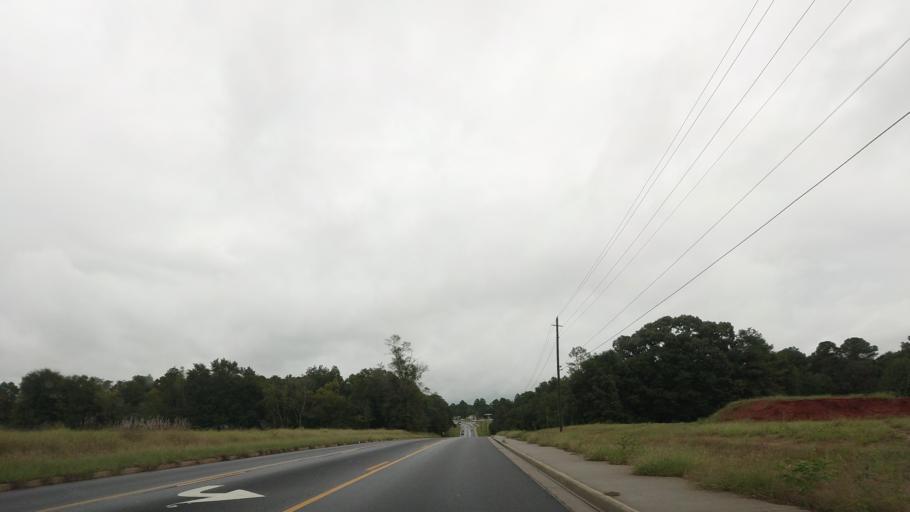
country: US
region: Georgia
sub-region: Houston County
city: Centerville
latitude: 32.5716
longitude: -83.6585
